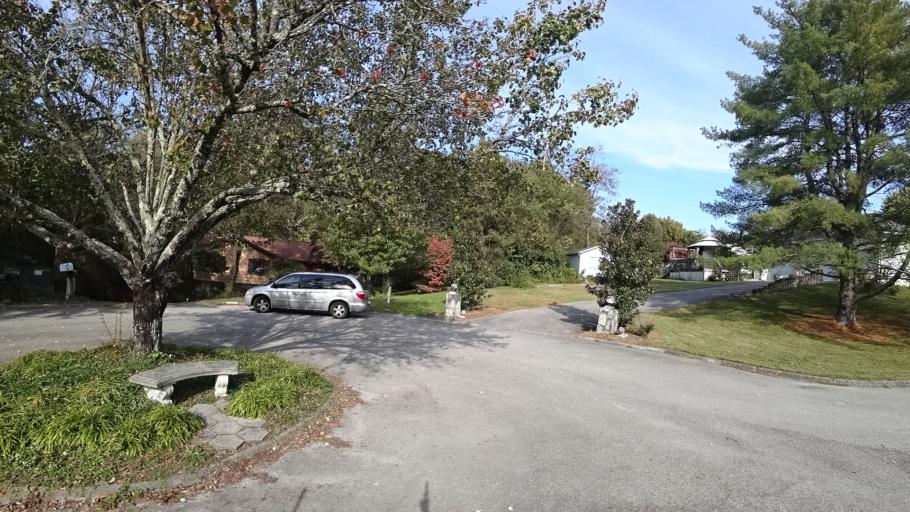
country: US
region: Tennessee
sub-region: Knox County
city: Farragut
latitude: 35.9158
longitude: -84.1681
